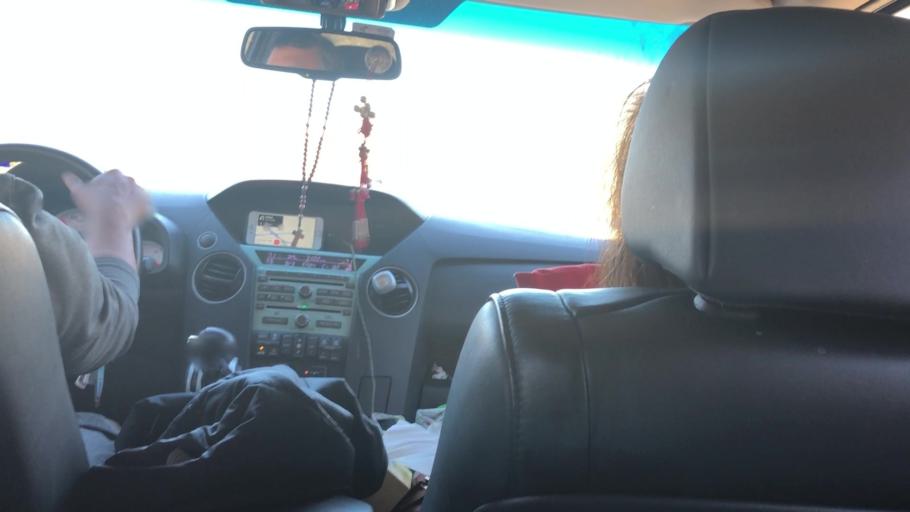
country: US
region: Louisiana
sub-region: Saint John the Baptist Parish
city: Montegut
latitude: 30.1056
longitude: -90.4933
